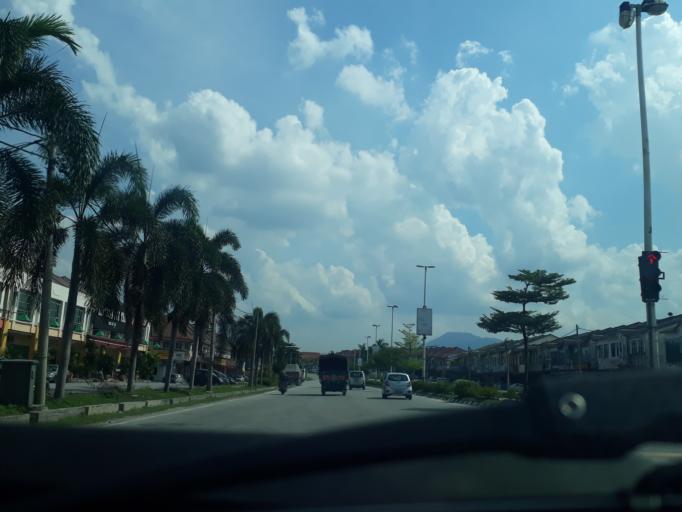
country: MY
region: Perak
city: Ipoh
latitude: 4.6419
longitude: 101.0955
